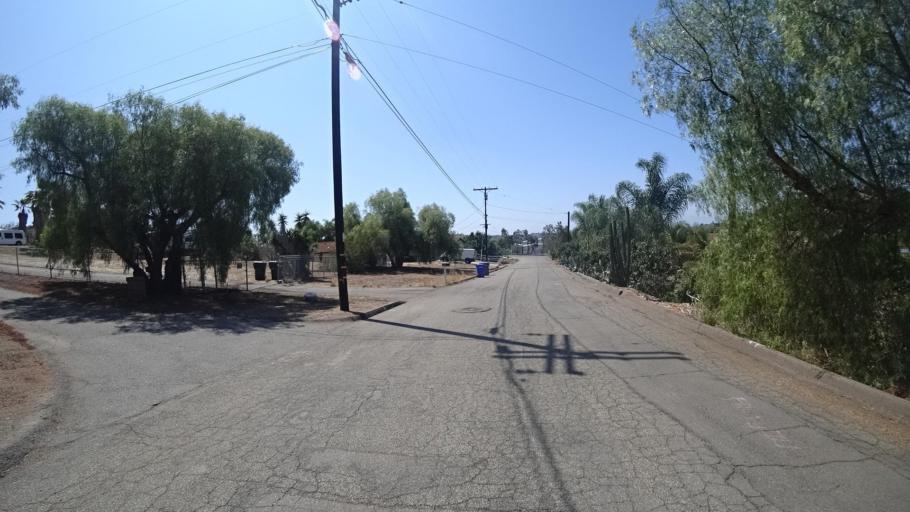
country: US
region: California
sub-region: San Diego County
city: Lake San Marcos
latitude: 33.1656
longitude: -117.1999
